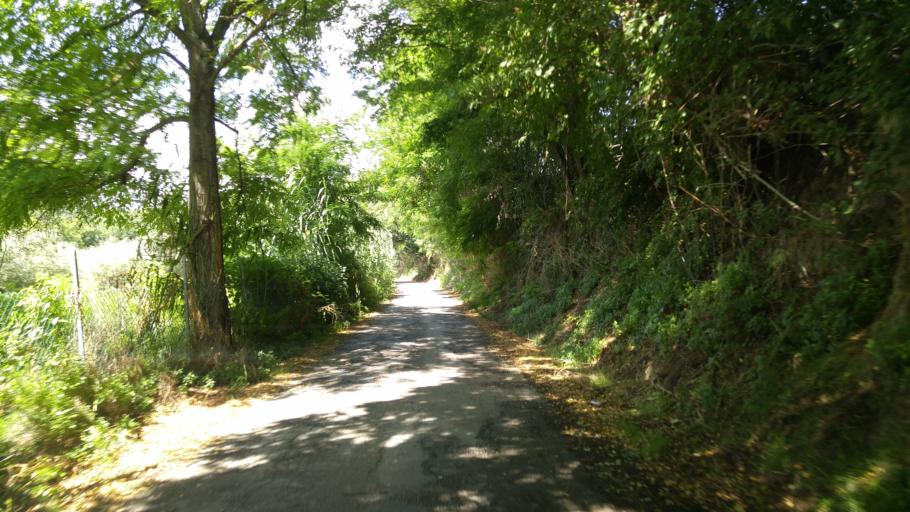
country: IT
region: The Marches
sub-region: Provincia di Pesaro e Urbino
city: Centinarola
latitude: 43.8158
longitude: 12.9716
